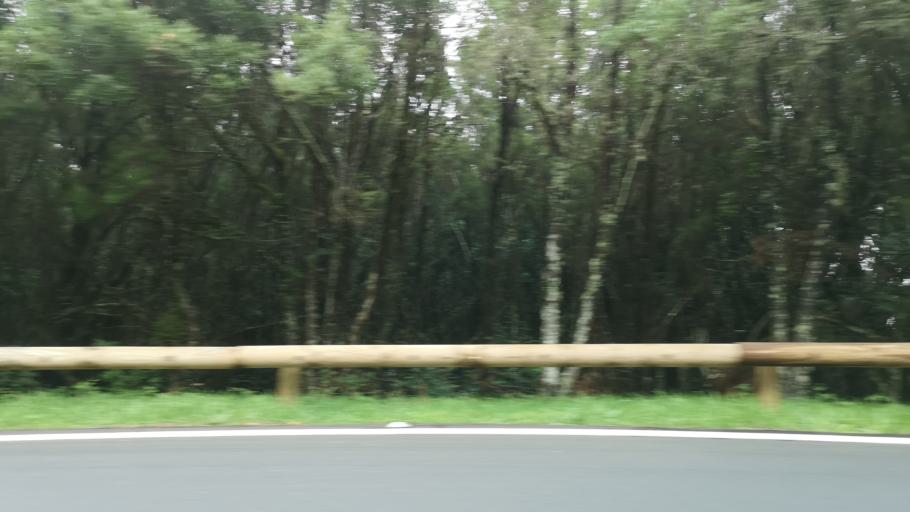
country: ES
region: Canary Islands
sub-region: Provincia de Santa Cruz de Tenerife
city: Vallehermosa
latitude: 28.1349
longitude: -17.2794
